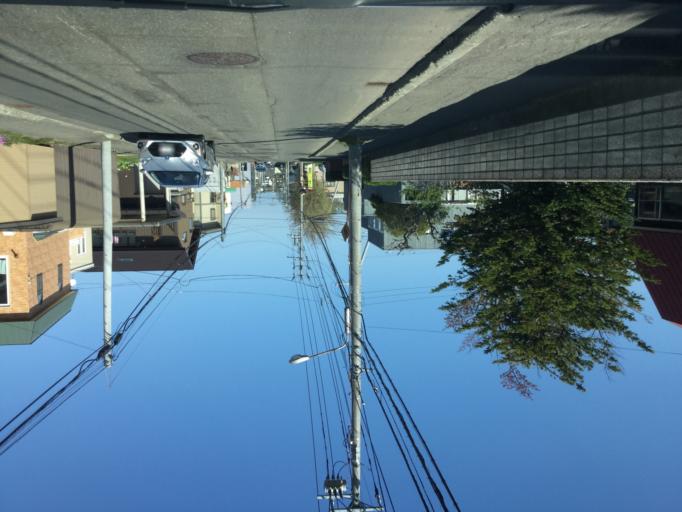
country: JP
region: Hokkaido
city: Sapporo
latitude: 43.0157
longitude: 141.4213
